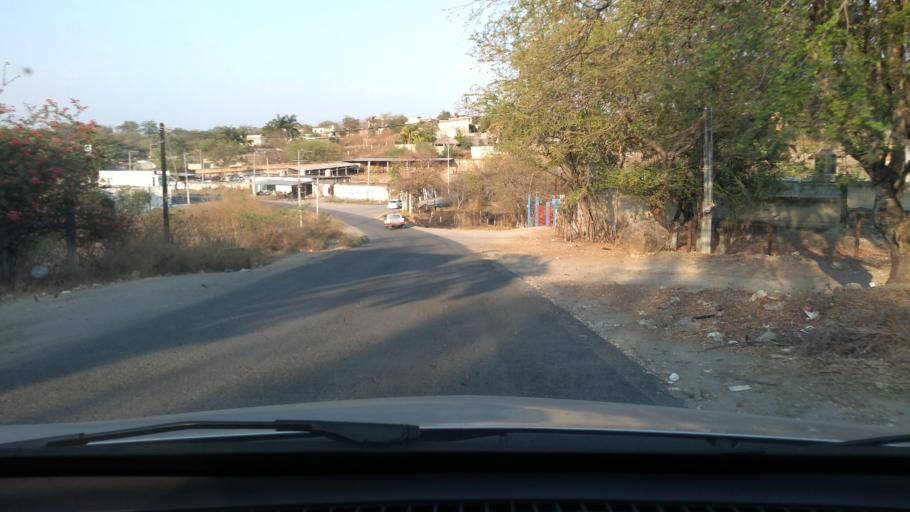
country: MX
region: Morelos
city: Puente de Ixtla
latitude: 18.6117
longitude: -99.3133
